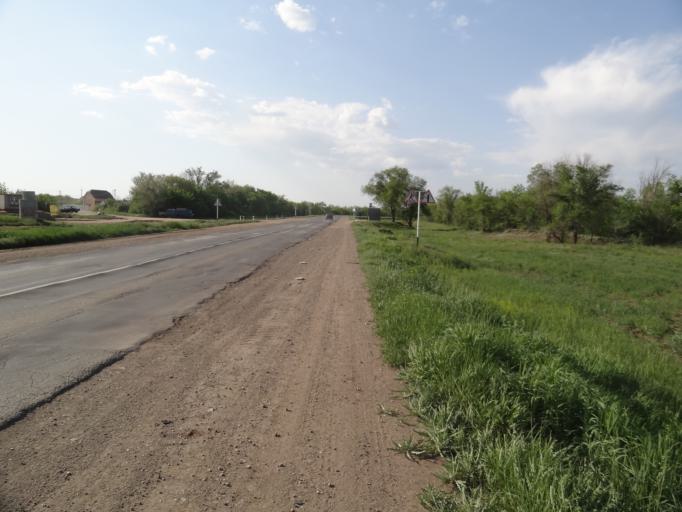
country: RU
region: Saratov
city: Privolzhskiy
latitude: 51.3524
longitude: 46.0450
